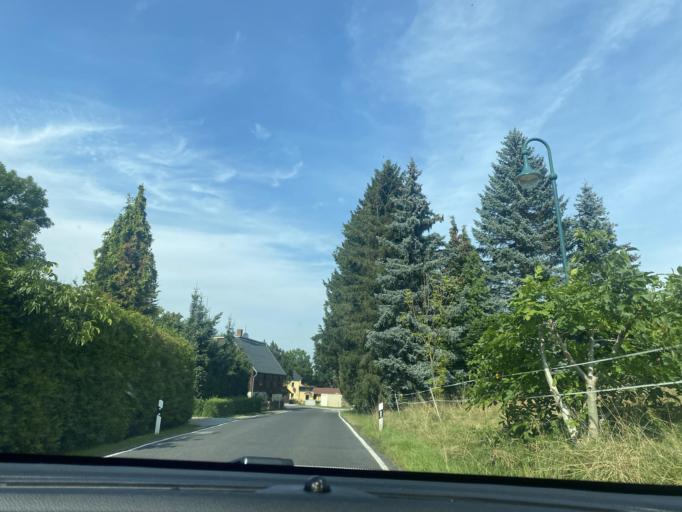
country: DE
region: Saxony
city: Sohland am Rotstein
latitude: 51.1087
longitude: 14.7822
